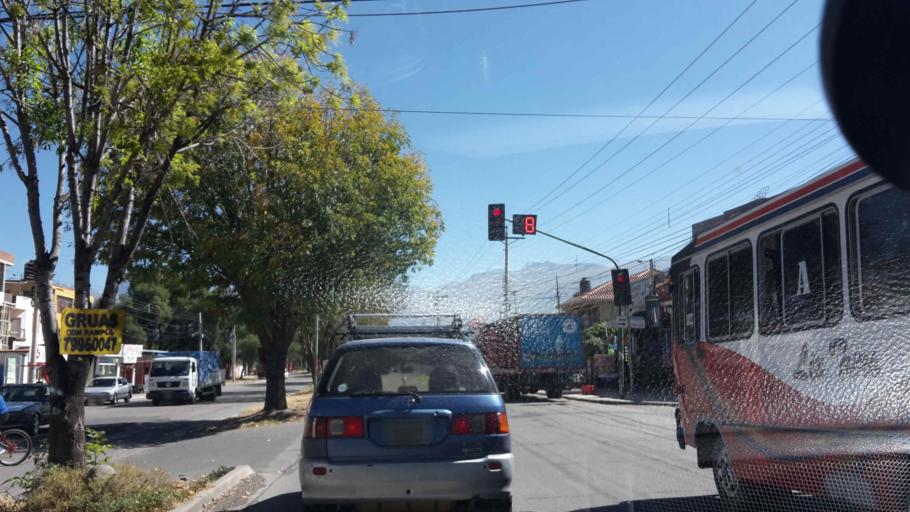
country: BO
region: Cochabamba
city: Cochabamba
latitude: -17.3556
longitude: -66.1774
